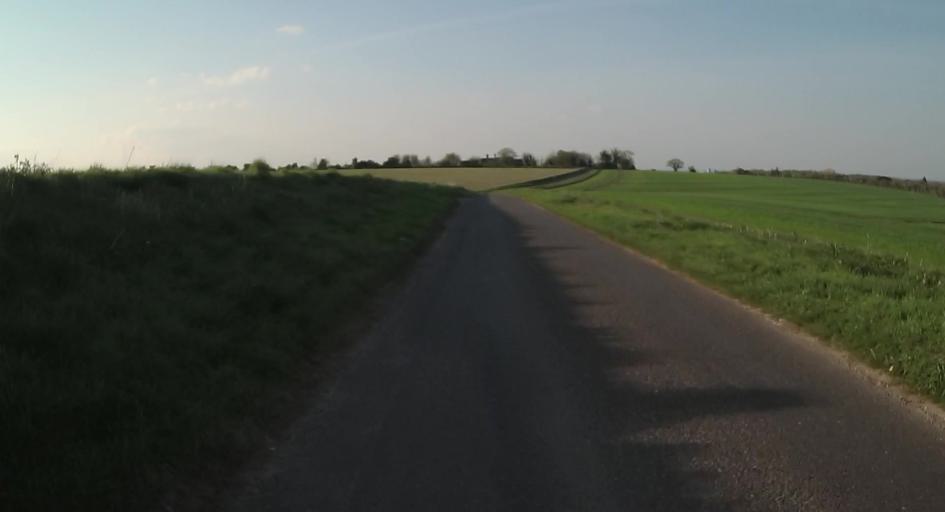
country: GB
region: England
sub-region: Hampshire
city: Basingstoke
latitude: 51.2270
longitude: -1.0914
